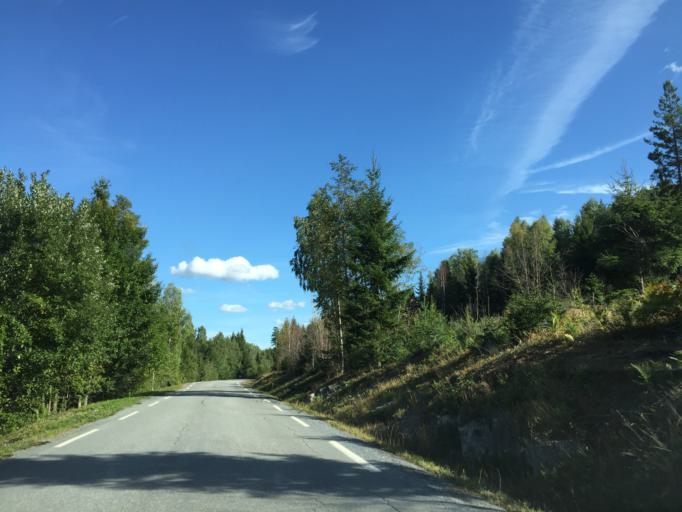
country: NO
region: Buskerud
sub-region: Ovre Eiker
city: Hokksund
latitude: 59.6620
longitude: 9.8949
